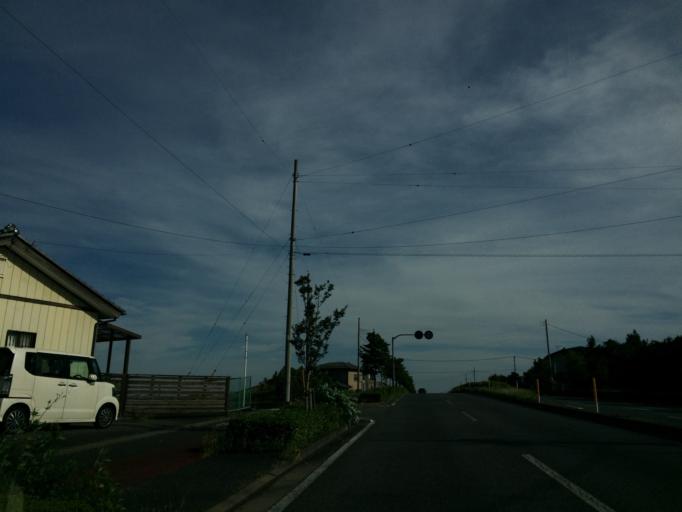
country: JP
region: Gunma
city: Shibukawa
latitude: 36.4894
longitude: 138.9969
